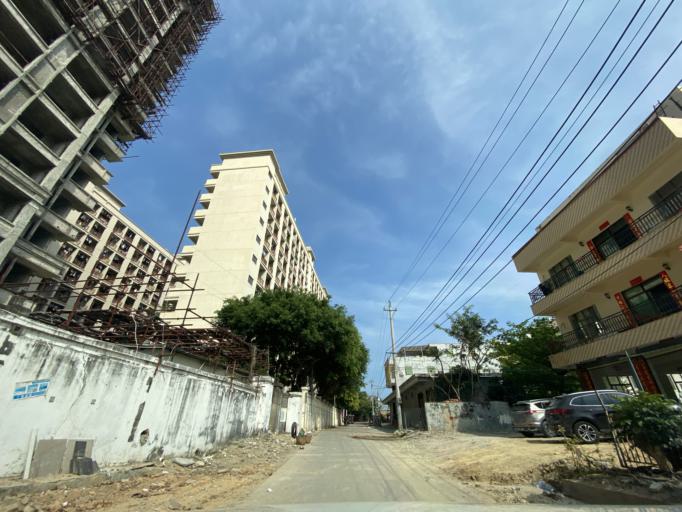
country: CN
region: Hainan
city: Yingzhou
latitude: 18.4043
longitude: 109.8410
